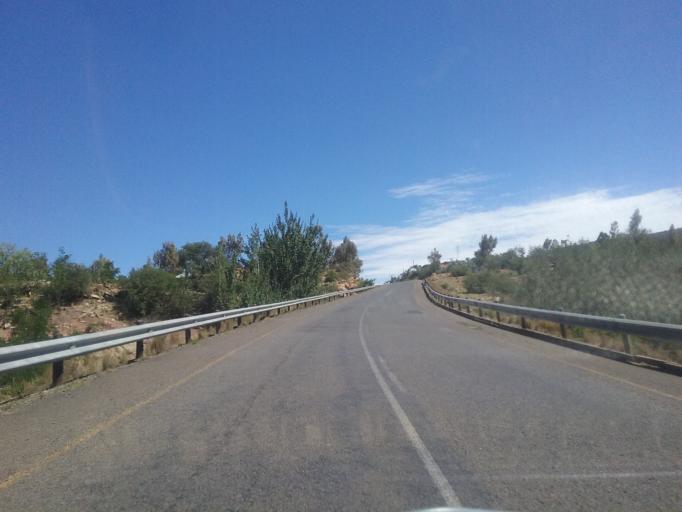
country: LS
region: Quthing
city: Quthing
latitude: -30.3661
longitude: 27.5507
